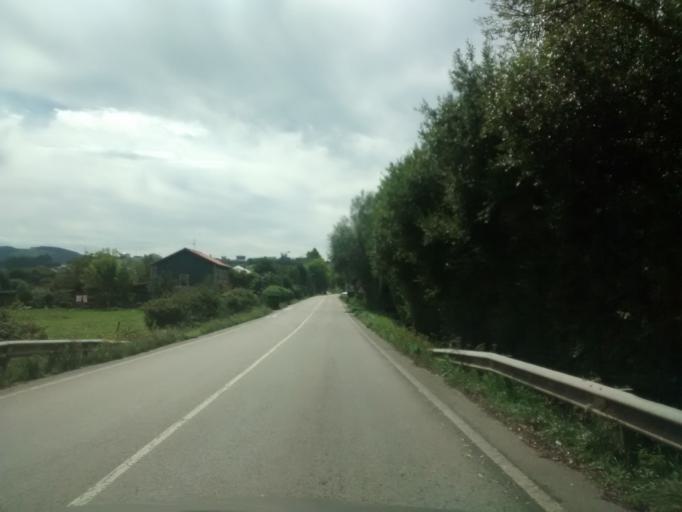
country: ES
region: Cantabria
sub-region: Provincia de Cantabria
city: Miengo
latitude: 43.4177
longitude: -3.9593
